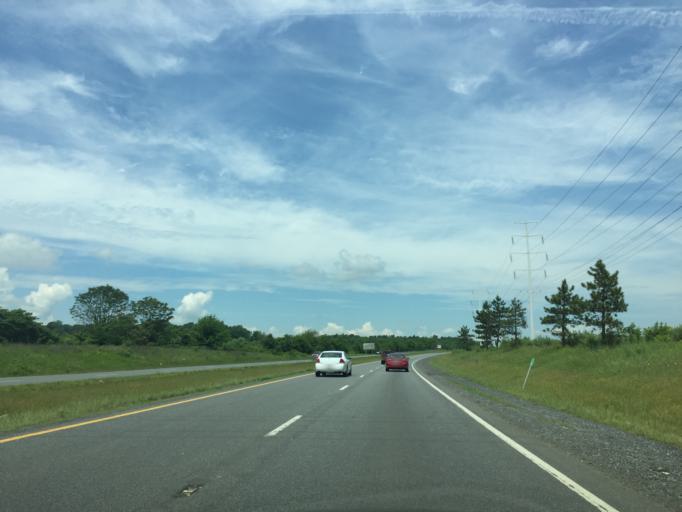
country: US
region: Virginia
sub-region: Frederick County
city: Stephens City
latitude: 39.1338
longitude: -78.2080
